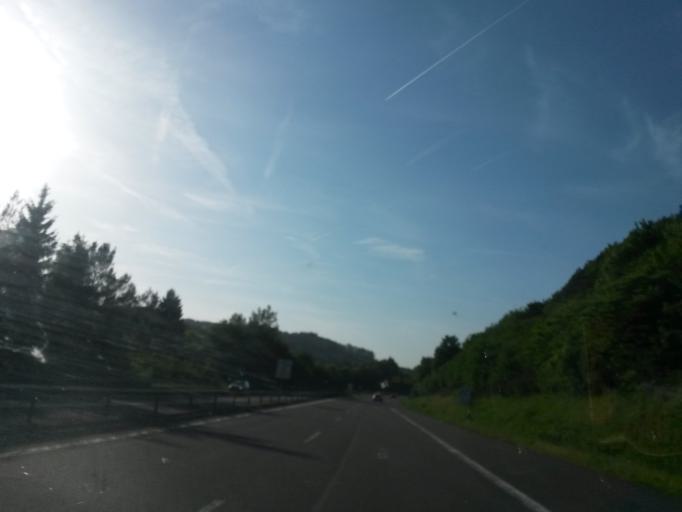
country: DE
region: North Rhine-Westphalia
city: Bergneustadt
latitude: 50.9932
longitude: 7.6418
